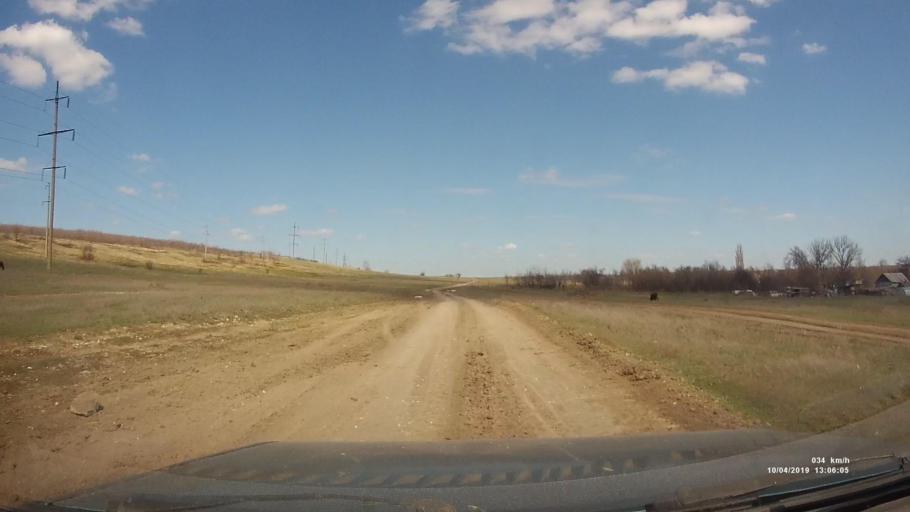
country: RU
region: Rostov
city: Masalovka
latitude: 48.3906
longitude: 40.2349
